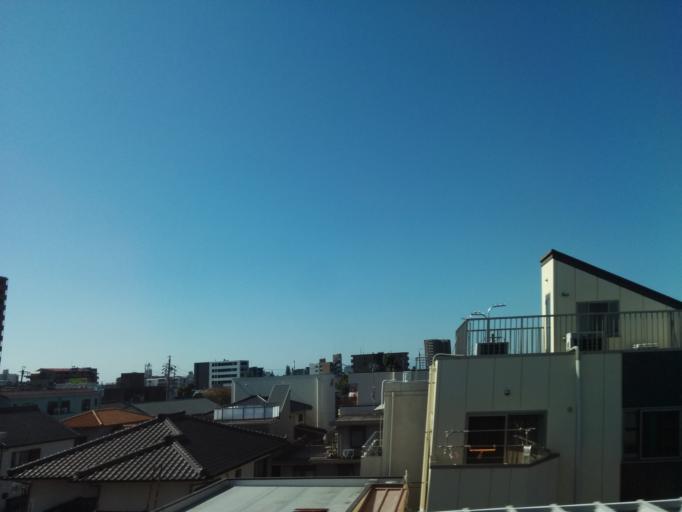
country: JP
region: Aichi
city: Nagoya-shi
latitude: 35.1246
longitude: 136.8876
